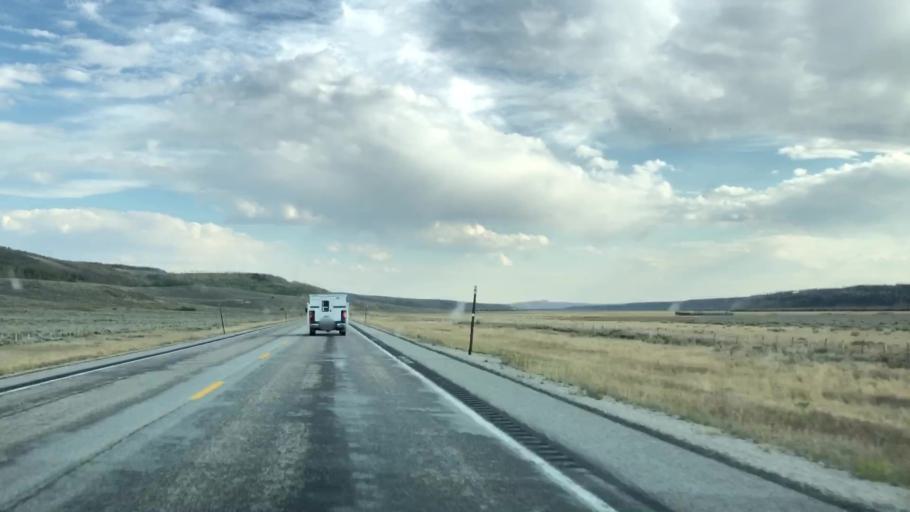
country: US
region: Wyoming
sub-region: Sublette County
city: Pinedale
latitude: 43.1023
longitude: -110.1700
